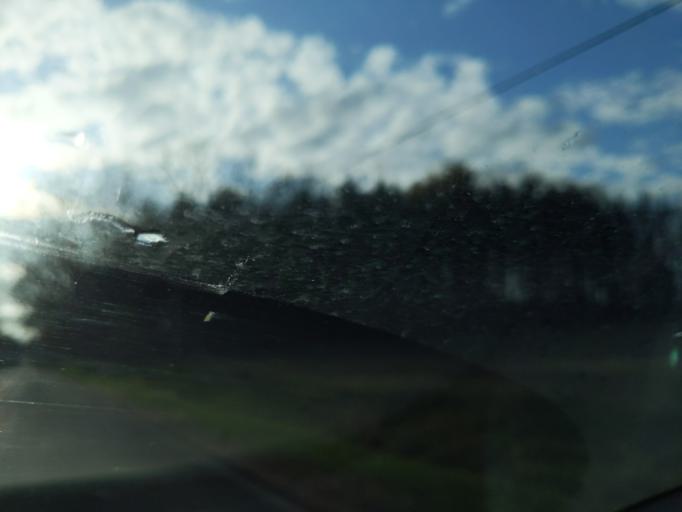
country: US
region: Michigan
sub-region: Ingham County
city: Leslie
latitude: 42.3933
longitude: -84.4327
